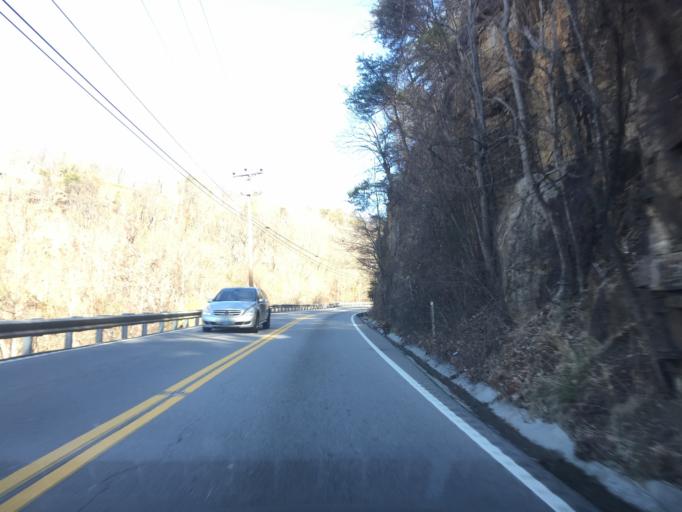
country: US
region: Tennessee
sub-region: Hamilton County
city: Signal Mountain
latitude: 35.1135
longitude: -85.3551
